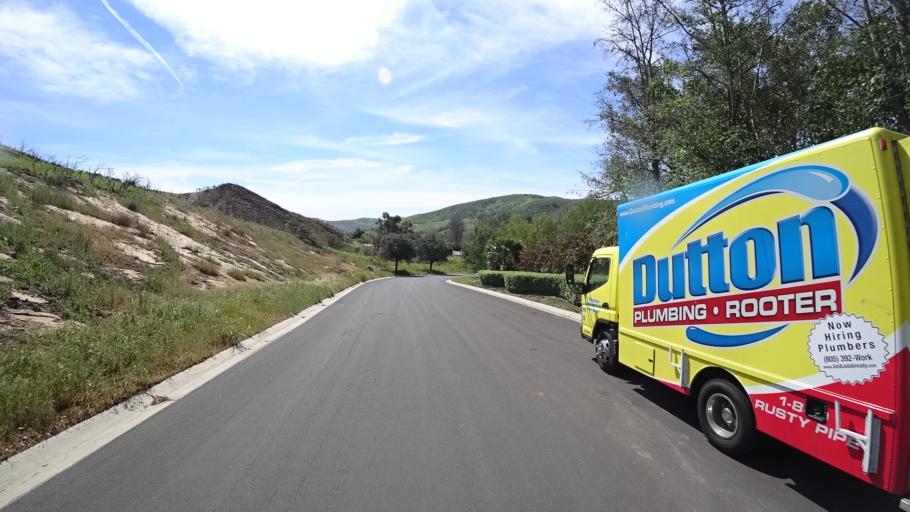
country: US
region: California
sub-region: Ventura County
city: Oak Park
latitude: 34.1936
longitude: -118.7990
